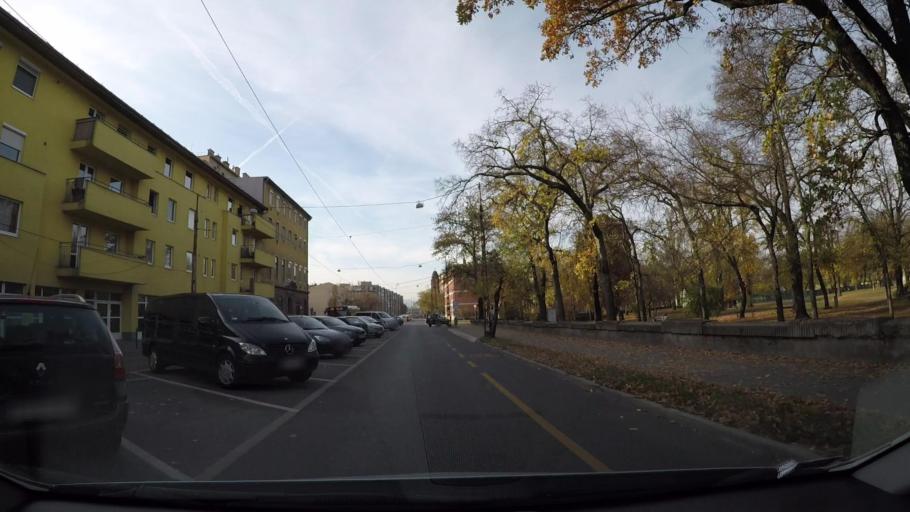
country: HU
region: Budapest
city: Budapest X. keruelet
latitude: 47.4813
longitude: 19.1367
